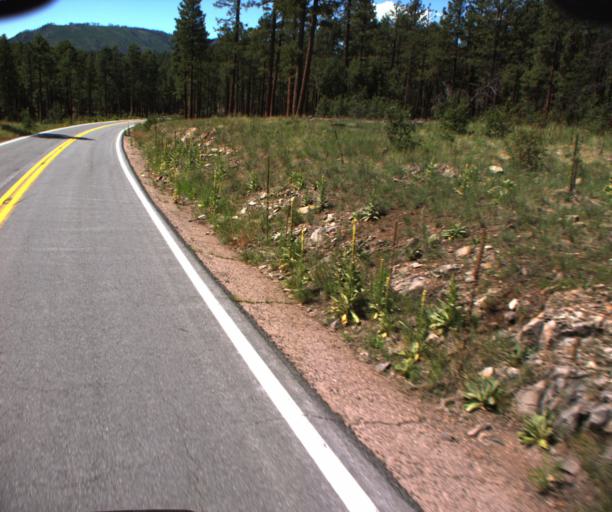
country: US
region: Arizona
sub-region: Apache County
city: Eagar
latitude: 33.7152
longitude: -109.1995
